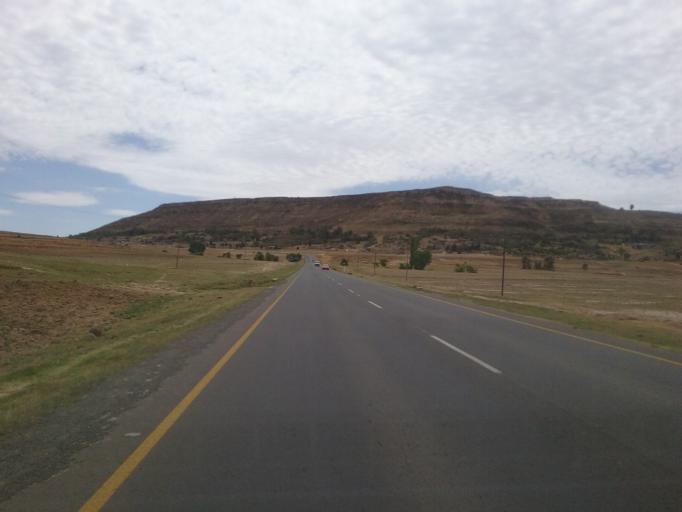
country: LS
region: Maseru
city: Nako
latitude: -29.6148
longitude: 27.4995
